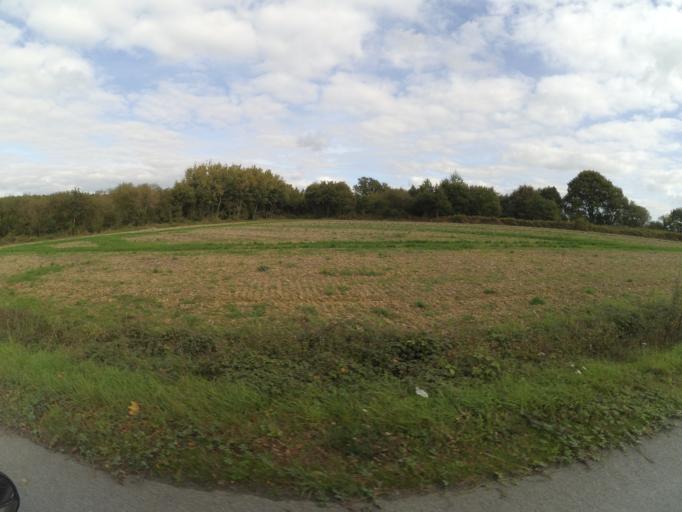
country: FR
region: Pays de la Loire
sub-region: Departement de la Loire-Atlantique
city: Bouvron
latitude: 47.4847
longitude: -1.8478
